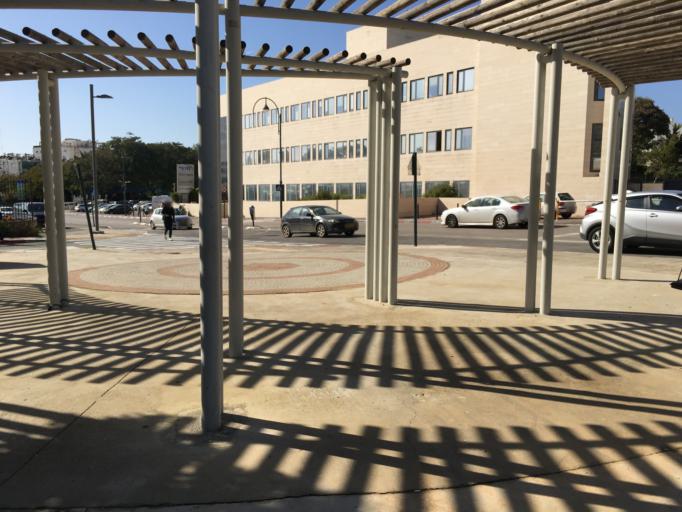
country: IL
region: Tel Aviv
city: Ramat HaSharon
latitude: 32.1386
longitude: 34.8446
